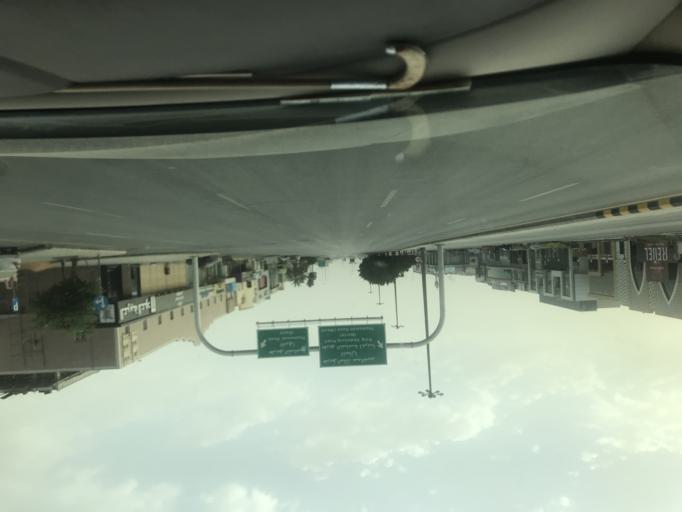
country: SA
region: Ar Riyad
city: Riyadh
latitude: 24.7942
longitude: 46.6564
